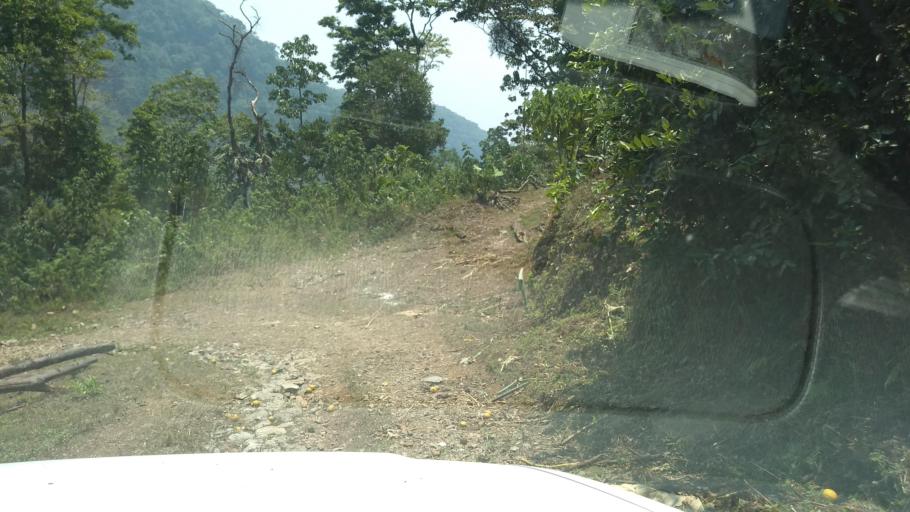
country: MX
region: Veracruz
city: Motzorongo
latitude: 18.6064
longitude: -96.7612
